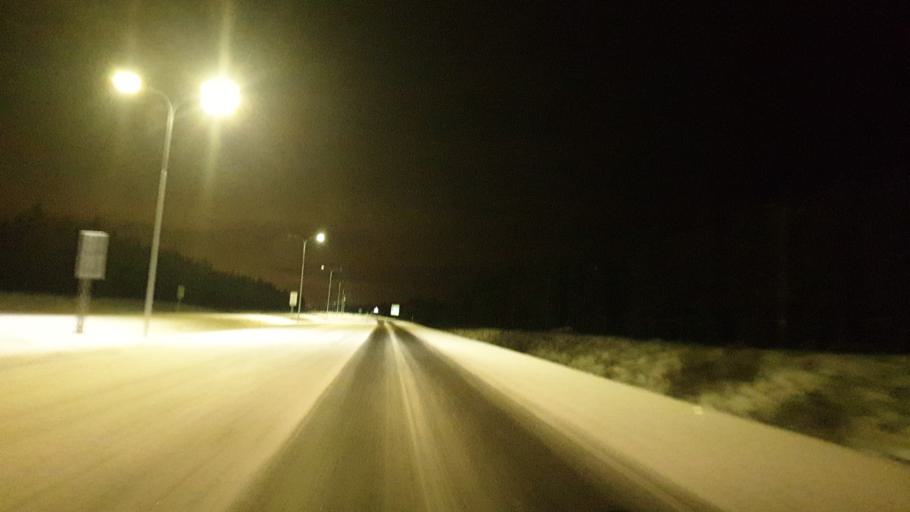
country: FI
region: Northern Ostrobothnia
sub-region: Oulu
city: Haukipudas
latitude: 65.1798
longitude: 25.4267
